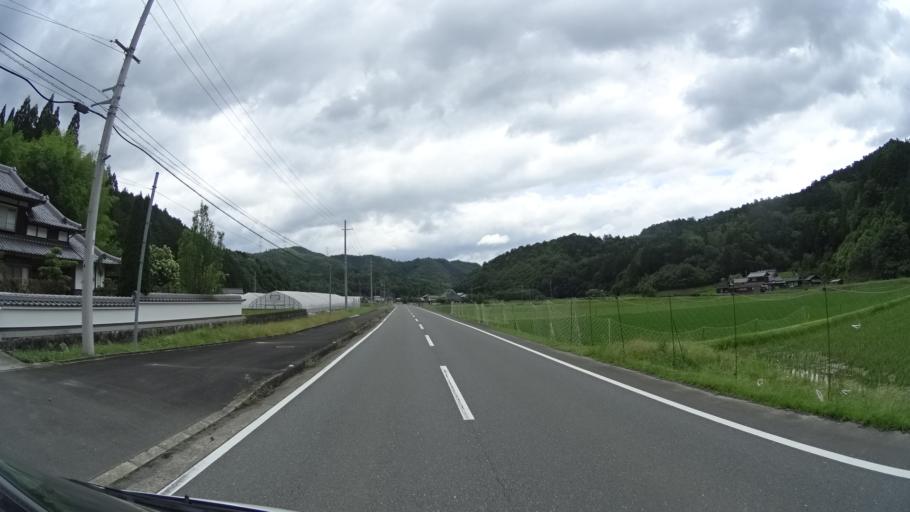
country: JP
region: Kyoto
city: Kameoka
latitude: 35.0863
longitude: 135.4181
